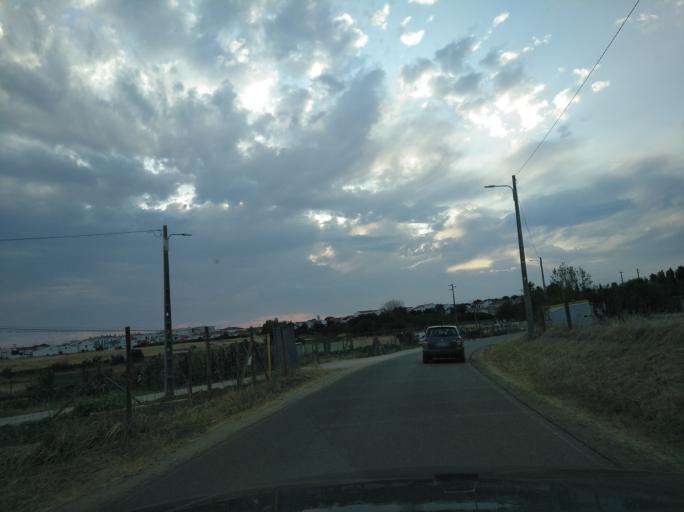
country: PT
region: Portalegre
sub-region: Campo Maior
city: Campo Maior
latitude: 39.0177
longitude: -7.0551
